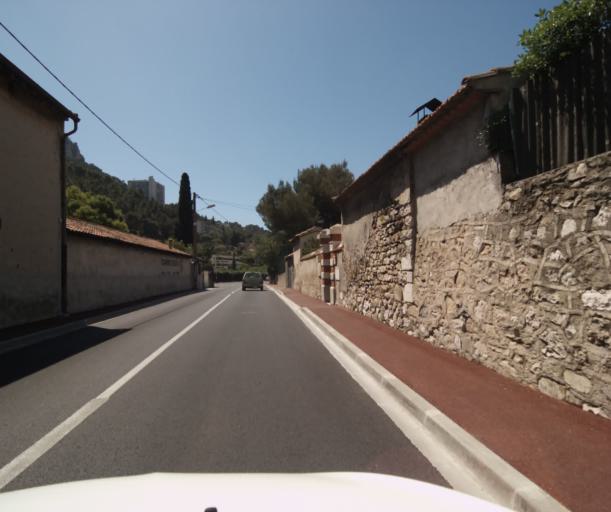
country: FR
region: Provence-Alpes-Cote d'Azur
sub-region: Departement du Var
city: Le Revest-les-Eaux
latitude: 43.1528
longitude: 5.9151
